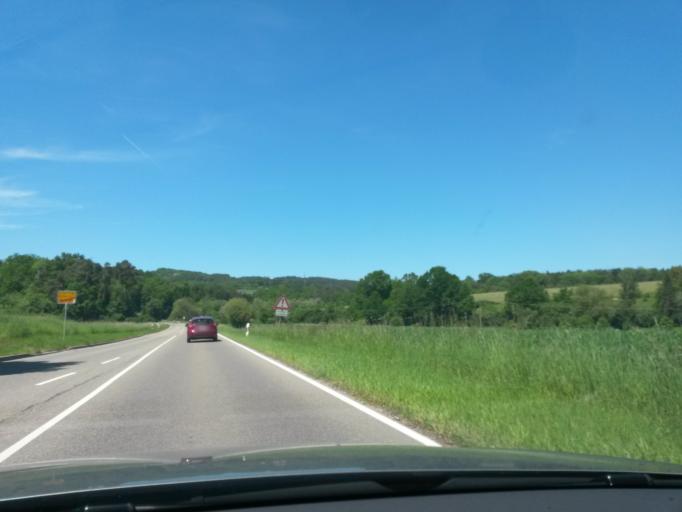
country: DE
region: Baden-Wuerttemberg
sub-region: Regierungsbezirk Stuttgart
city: Weil der Stadt
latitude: 48.7730
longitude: 8.8437
